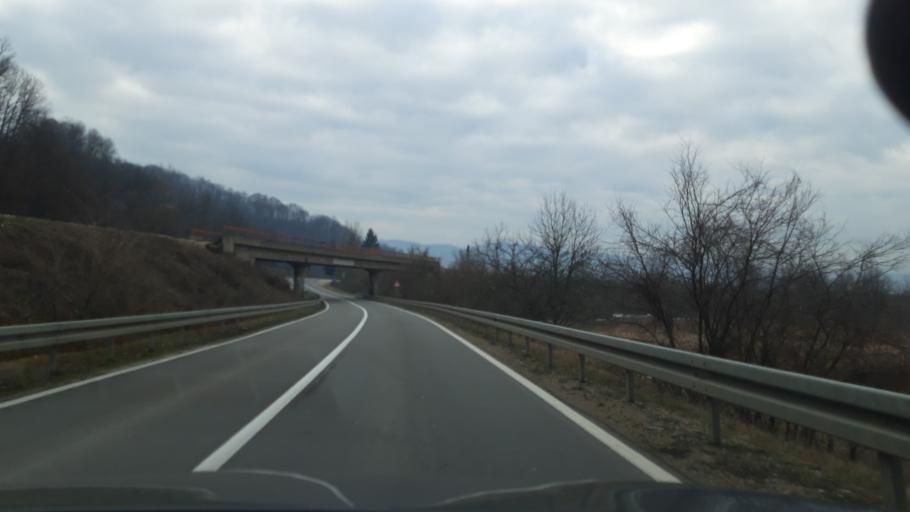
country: BA
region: Republika Srpska
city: Zvornik
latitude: 44.4293
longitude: 19.1504
